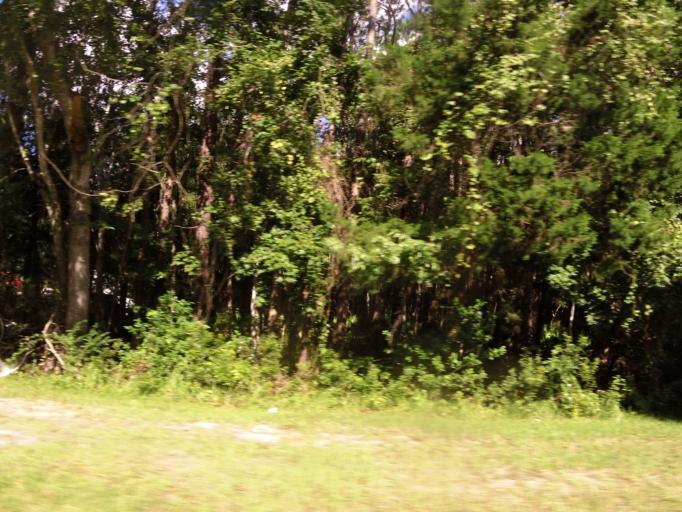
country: US
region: Georgia
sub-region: Camden County
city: Kingsland
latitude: 30.8118
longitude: -81.6925
